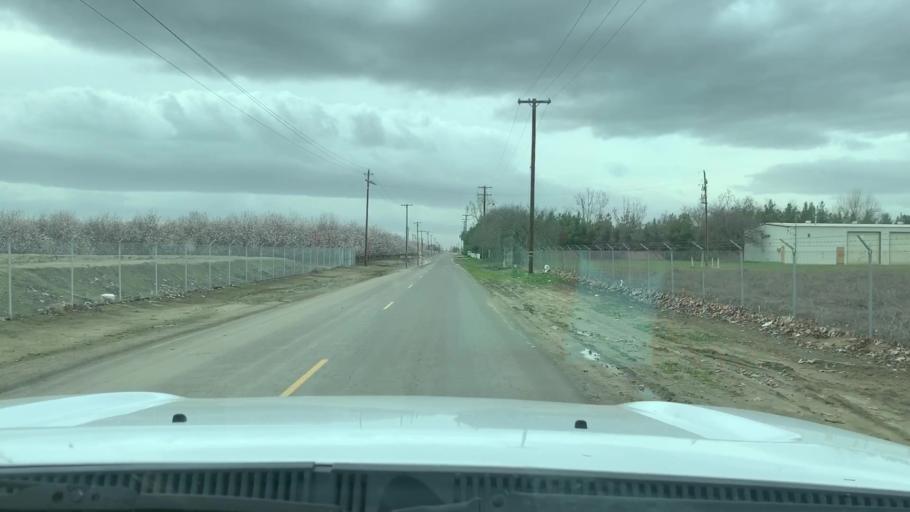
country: US
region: California
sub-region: Kern County
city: Shafter
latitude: 35.5292
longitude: -119.2649
